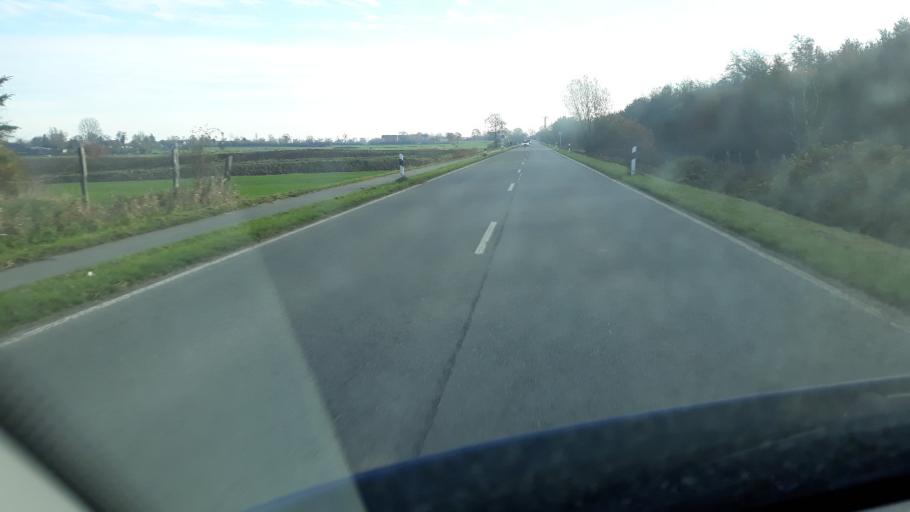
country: DE
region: Schleswig-Holstein
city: Maasholm
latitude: 54.6612
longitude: 9.9930
